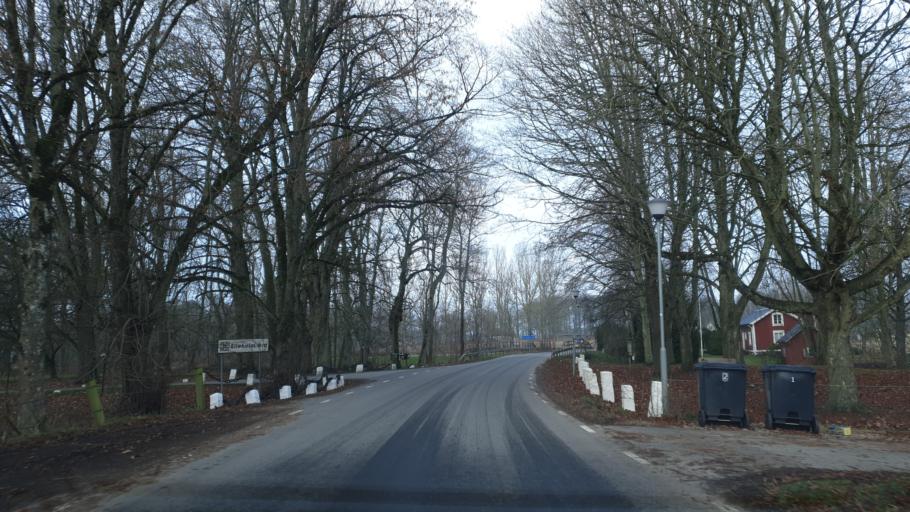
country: SE
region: Blekinge
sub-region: Karlshamns Kommun
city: Morrum
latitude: 56.1636
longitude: 14.7512
